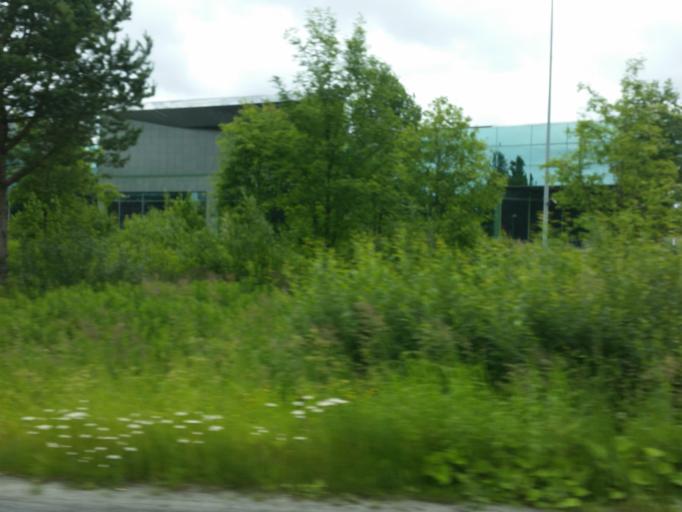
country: FI
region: Northern Savo
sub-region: Kuopio
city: Kuopio
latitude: 62.8861
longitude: 27.6290
